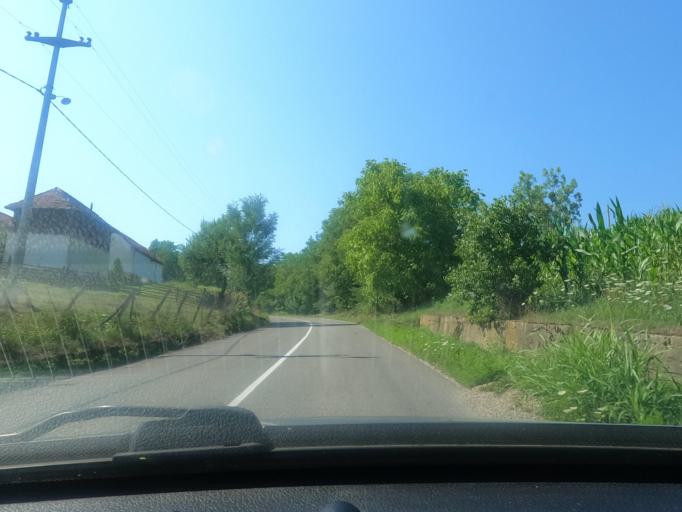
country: RS
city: Kozjak
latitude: 44.5464
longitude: 19.2970
